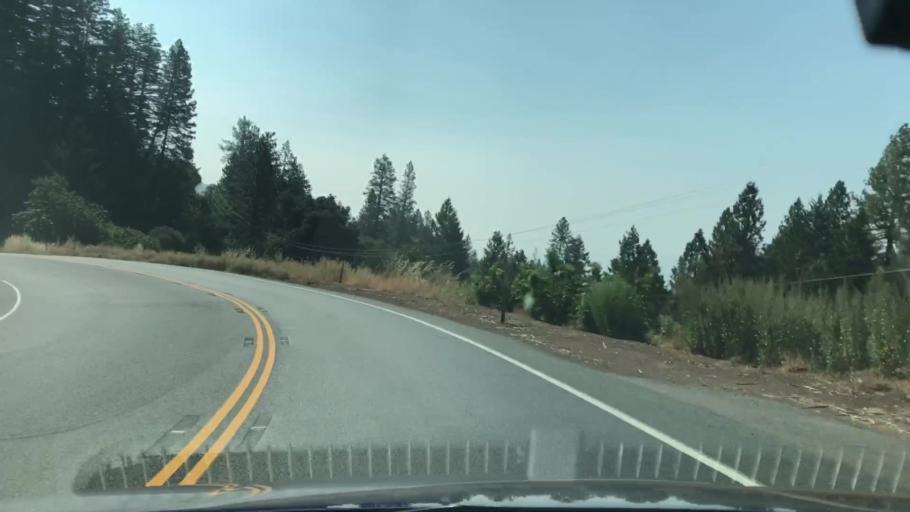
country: US
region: California
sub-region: Napa County
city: Calistoga
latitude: 38.6511
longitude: -122.5996
